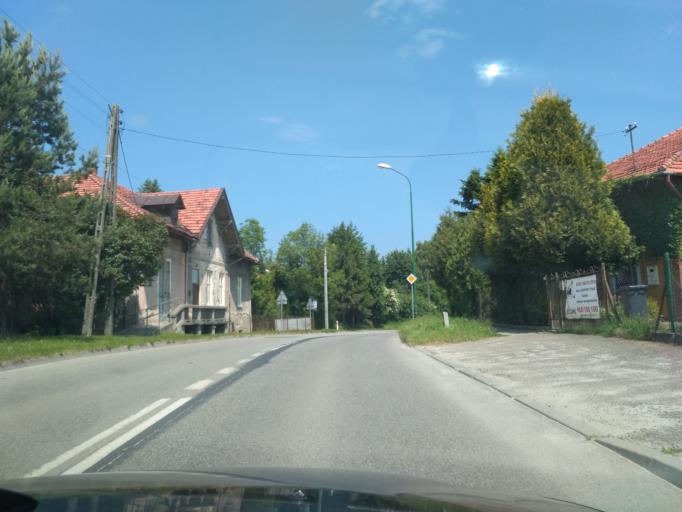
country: PL
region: Subcarpathian Voivodeship
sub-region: Powiat lancucki
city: Lancut
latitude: 50.0583
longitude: 22.2242
